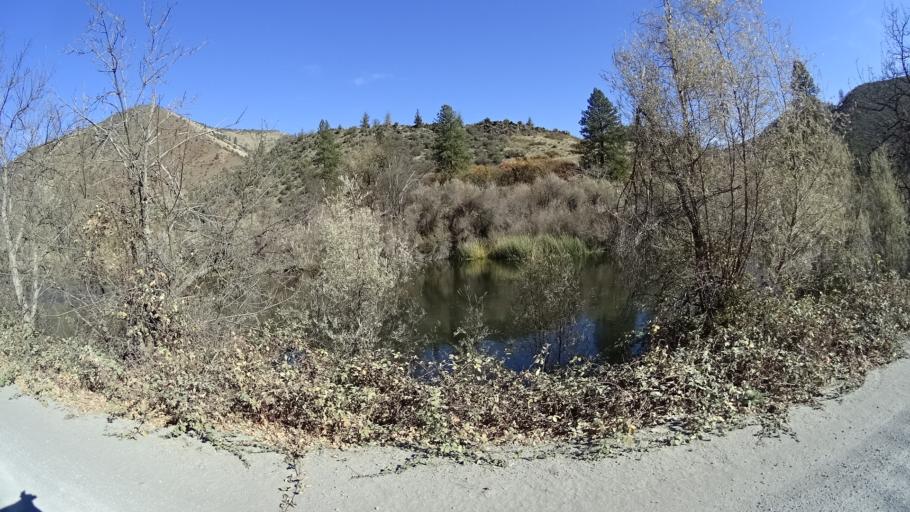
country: US
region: California
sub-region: Siskiyou County
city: Yreka
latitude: 41.8267
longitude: -122.6613
